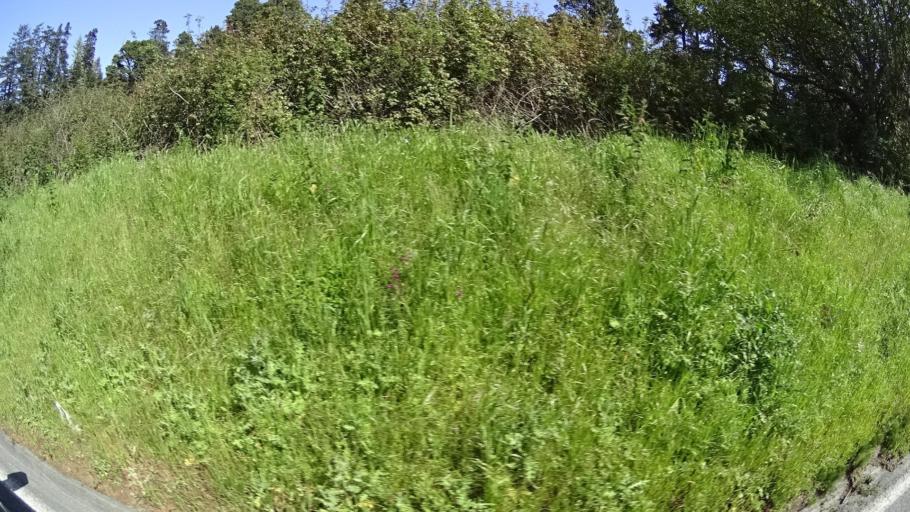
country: US
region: California
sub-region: Humboldt County
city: Hydesville
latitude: 40.5514
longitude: -124.1052
